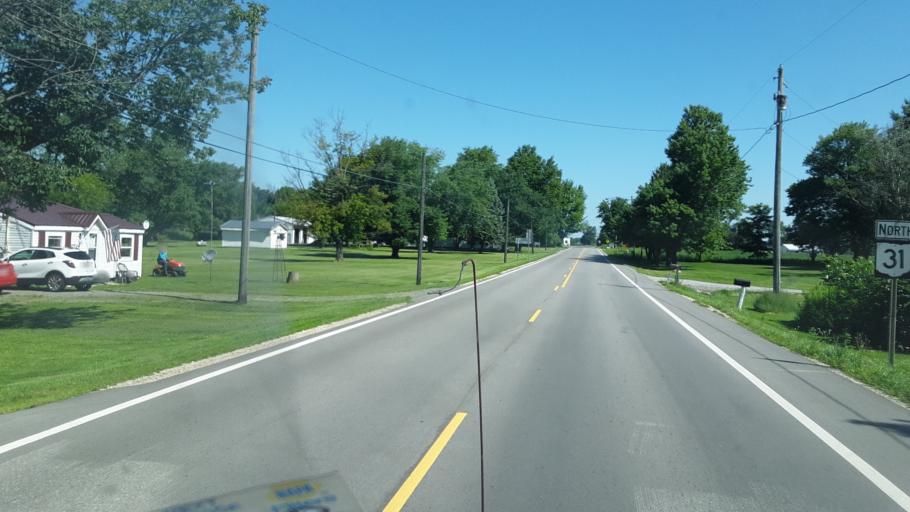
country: US
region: Ohio
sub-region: Union County
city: Richwood
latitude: 40.4019
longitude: -83.4118
